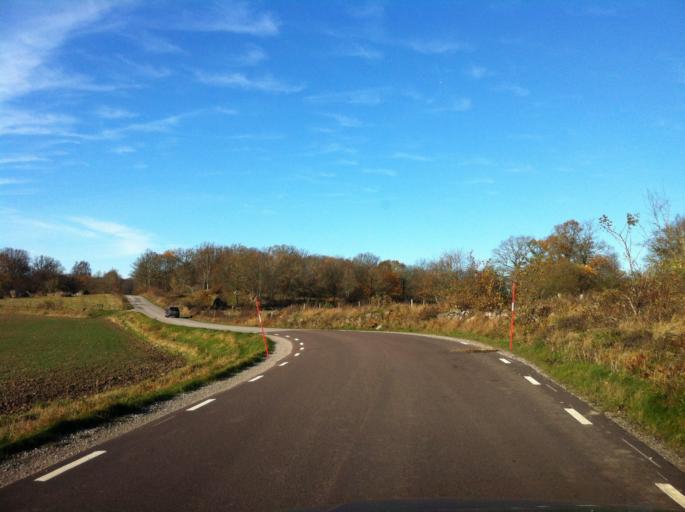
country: SE
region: Blekinge
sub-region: Ronneby Kommun
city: Brakne-Hoby
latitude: 56.1815
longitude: 15.1179
